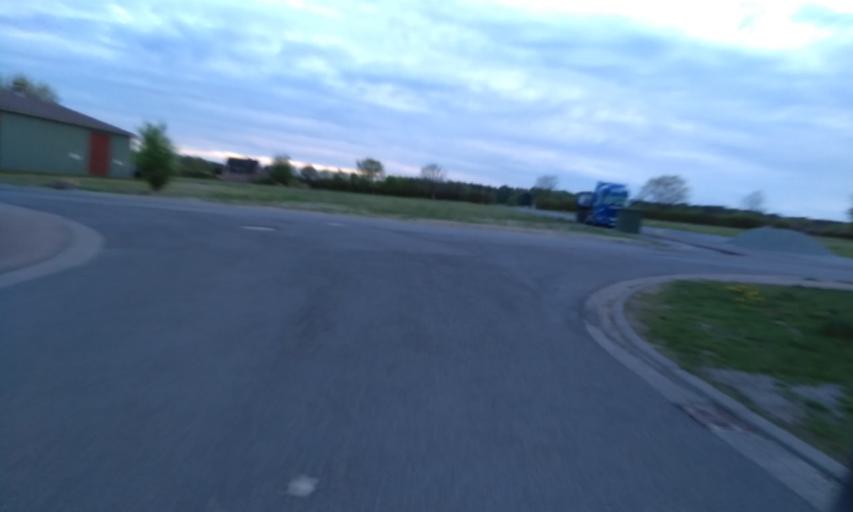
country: DE
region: Lower Saxony
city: Horneburg
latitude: 53.5085
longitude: 9.5667
